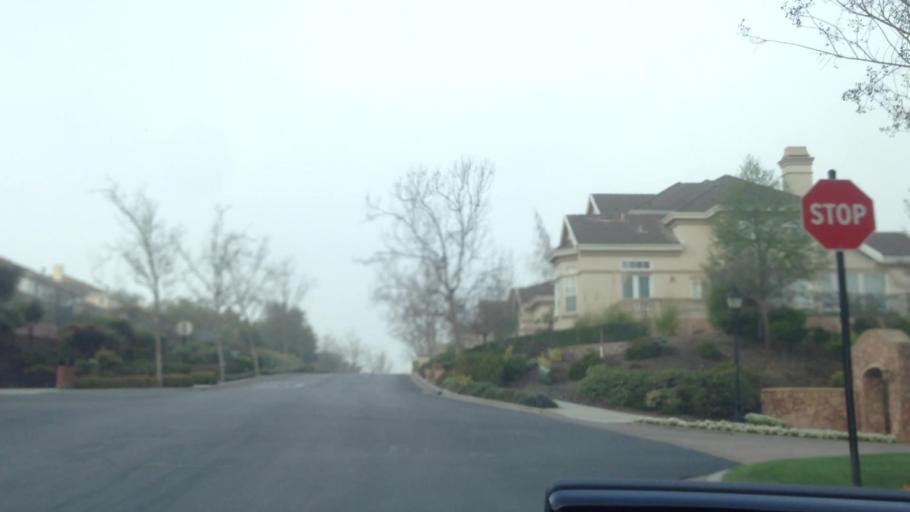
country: US
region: California
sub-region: Santa Clara County
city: Seven Trees
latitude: 37.2718
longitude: -121.7674
